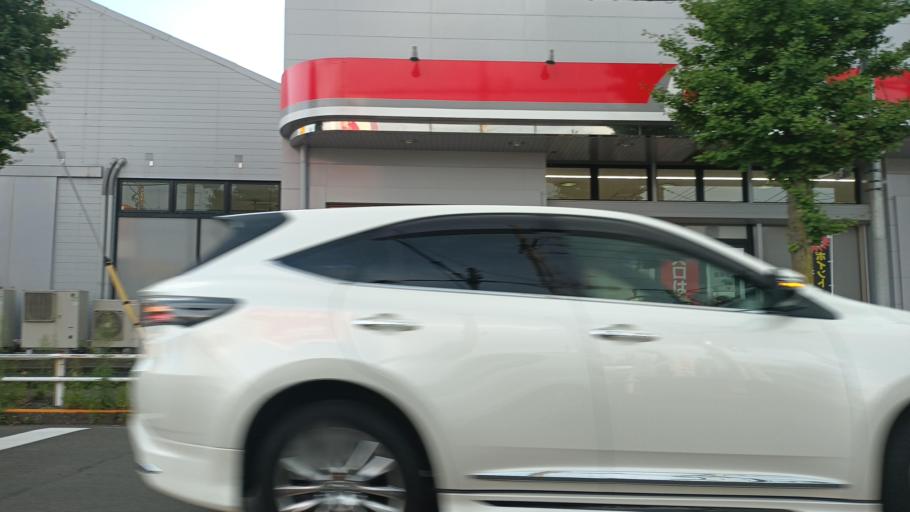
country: JP
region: Tokyo
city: Fussa
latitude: 35.7745
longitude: 139.3063
